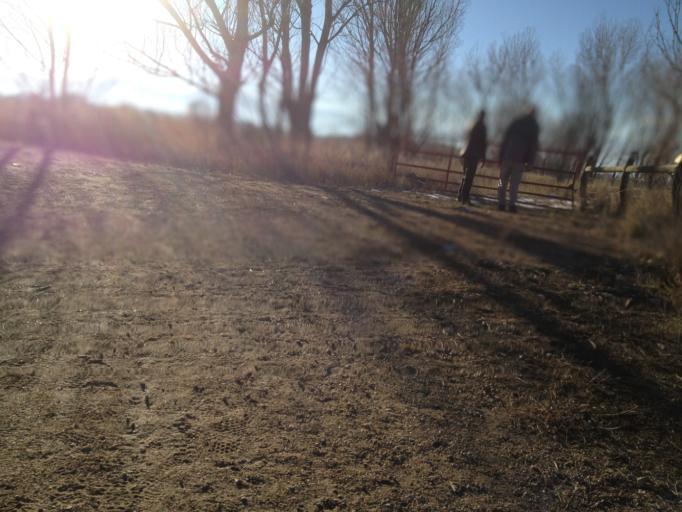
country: US
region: Colorado
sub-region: Boulder County
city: Gunbarrel
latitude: 40.0445
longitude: -105.1455
